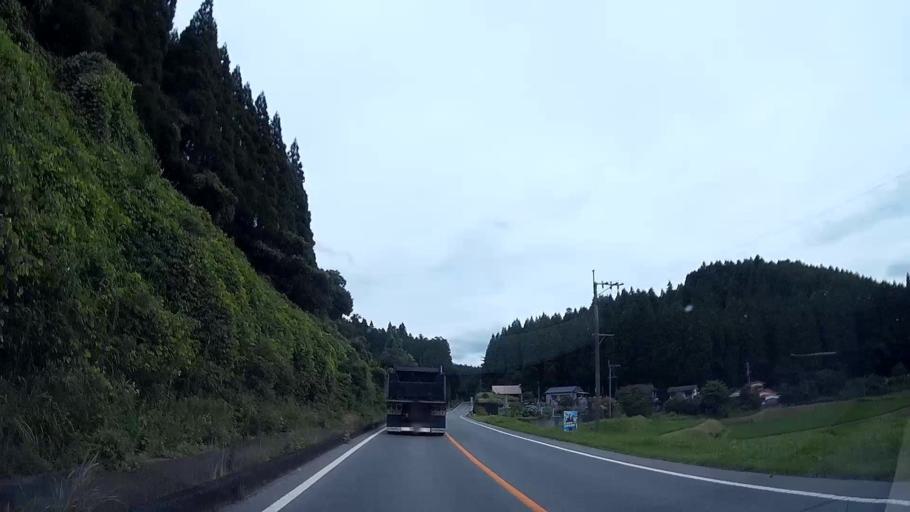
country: JP
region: Oita
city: Tsukawaki
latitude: 33.1250
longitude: 131.0528
